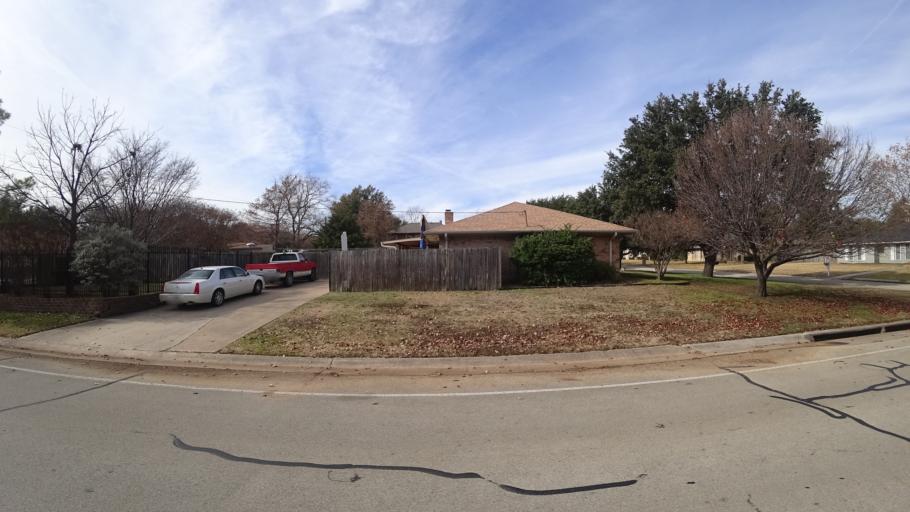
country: US
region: Texas
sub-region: Denton County
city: Highland Village
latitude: 33.0800
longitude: -97.0451
